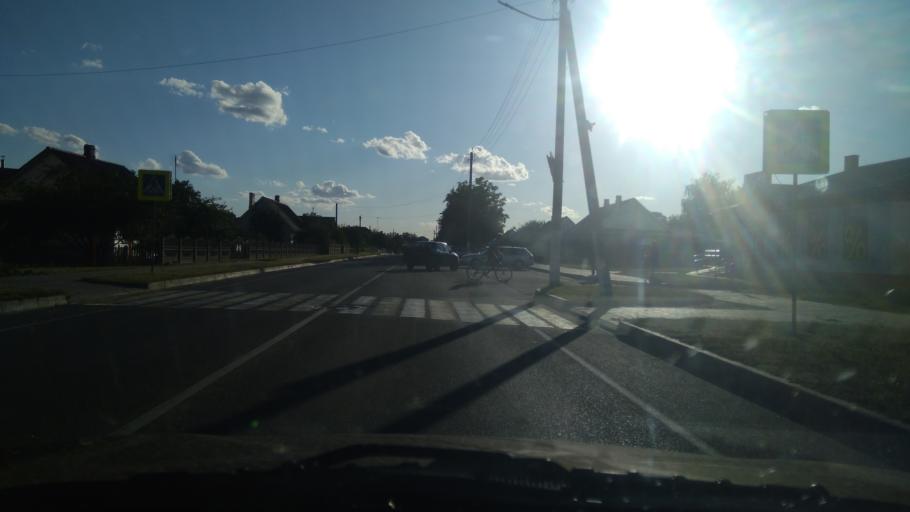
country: BY
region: Brest
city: Pruzhany
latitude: 52.5617
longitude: 24.4756
